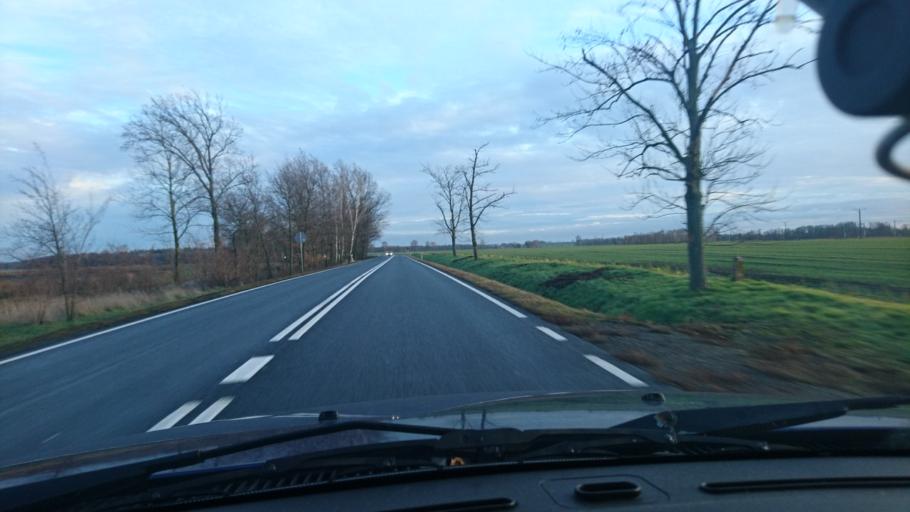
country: PL
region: Lodz Voivodeship
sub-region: Powiat wieruszowski
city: Boleslawiec
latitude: 51.1582
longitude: 18.1668
